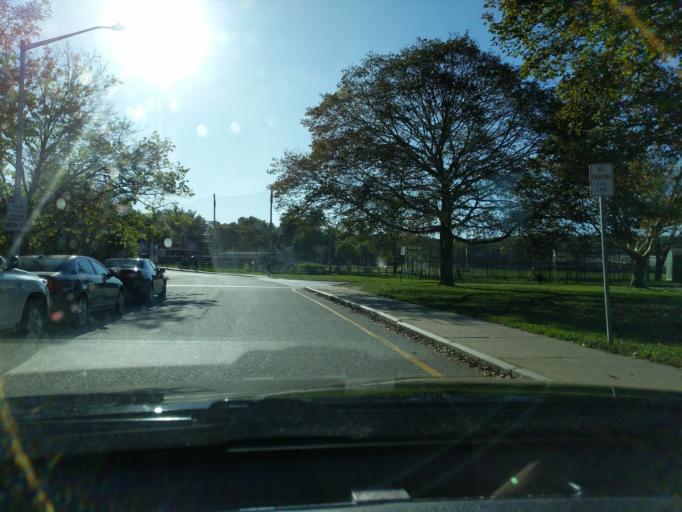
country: US
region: Massachusetts
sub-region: Middlesex County
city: Belmont
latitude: 42.3946
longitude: -71.1659
